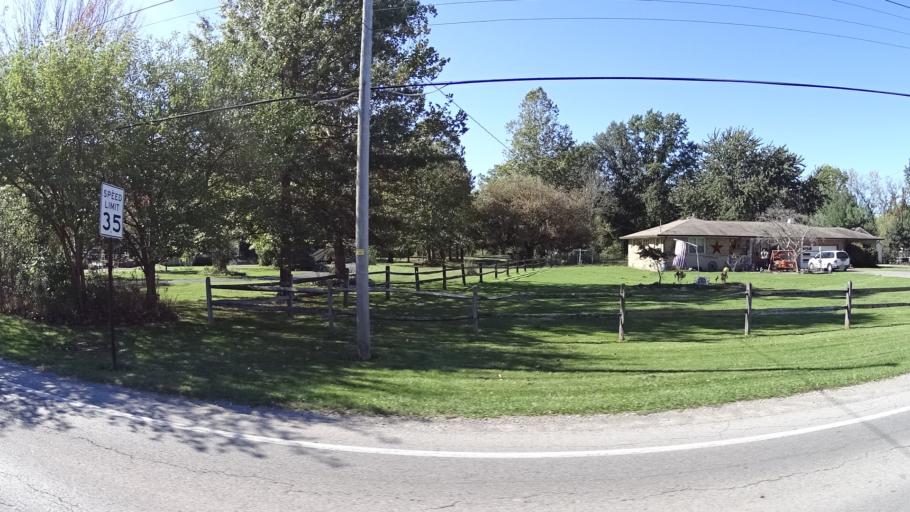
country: US
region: Ohio
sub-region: Lorain County
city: Amherst
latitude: 41.4222
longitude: -82.2263
